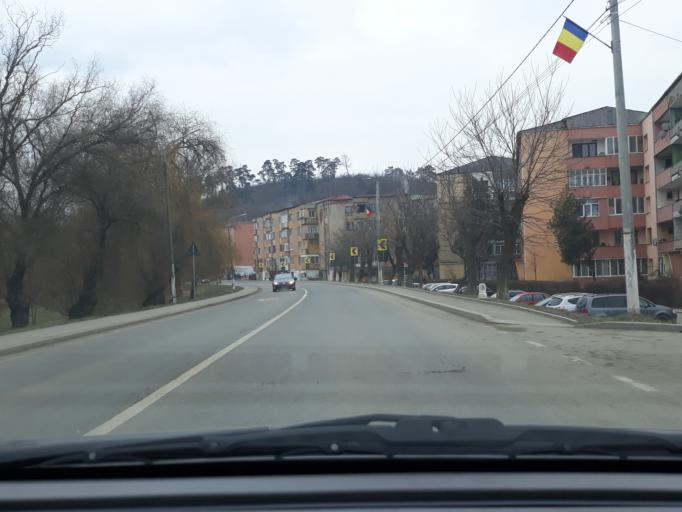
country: RO
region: Salaj
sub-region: Oras Simleu Silvaniei
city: Simleu Silvaniei
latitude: 47.2287
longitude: 22.7893
